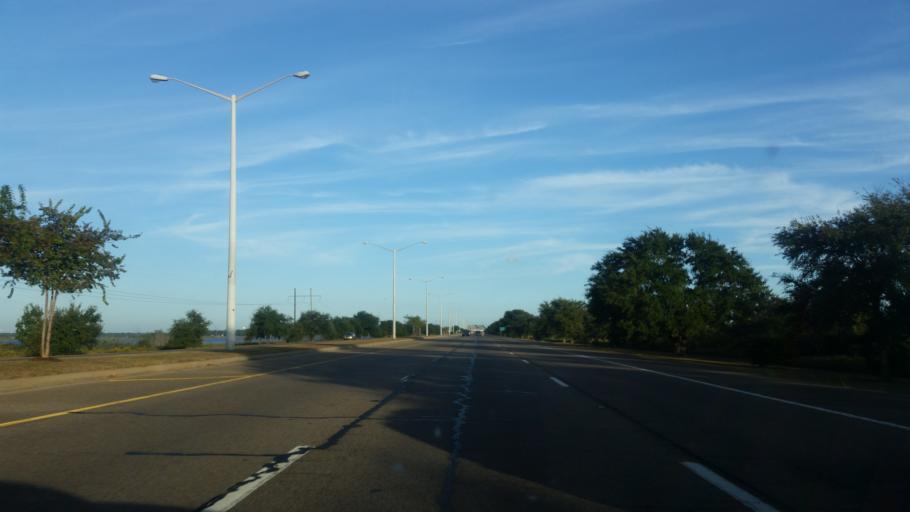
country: US
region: Mississippi
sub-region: Jackson County
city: Gautier
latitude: 30.3776
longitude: -88.5858
